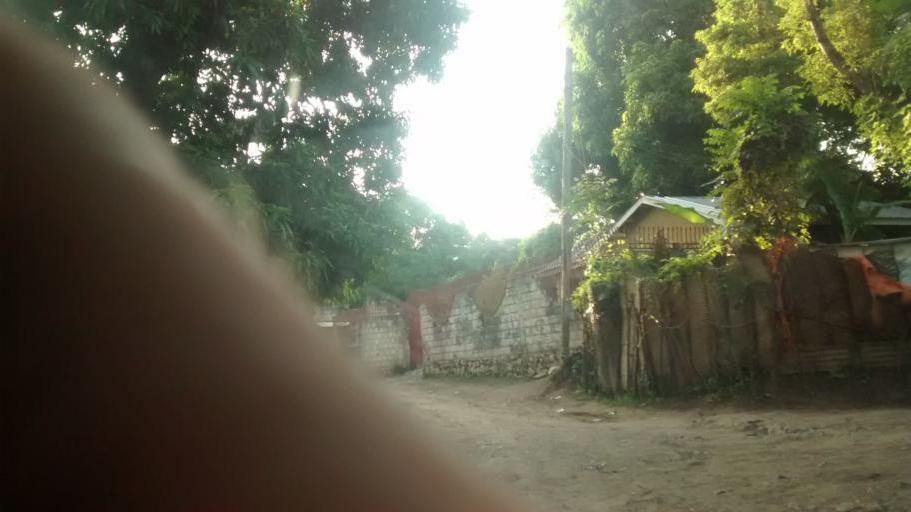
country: HT
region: Ouest
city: Grangwav
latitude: 18.4270
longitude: -72.7862
